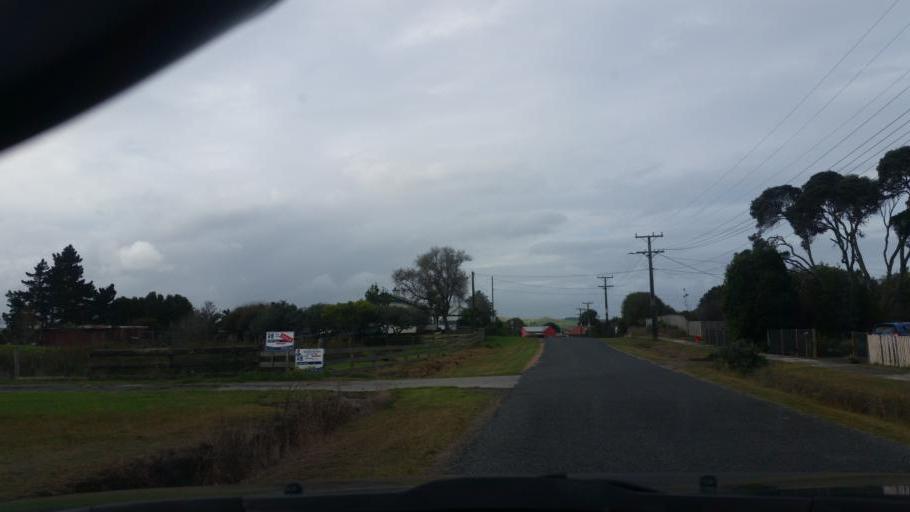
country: NZ
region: Northland
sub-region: Kaipara District
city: Dargaville
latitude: -36.0291
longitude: 173.9177
